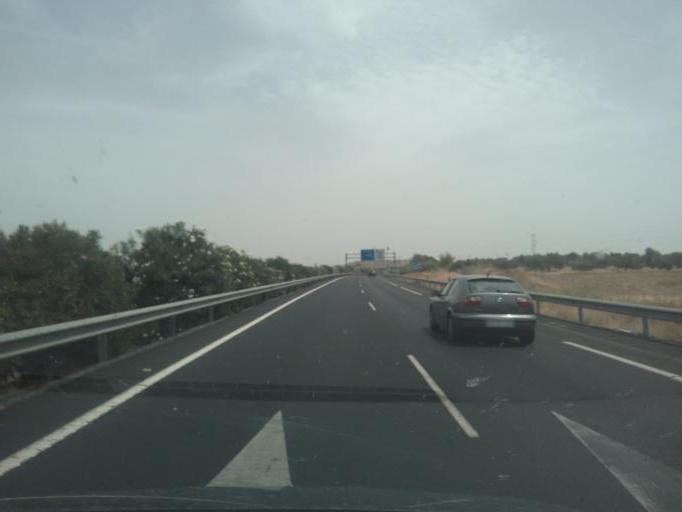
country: ES
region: Andalusia
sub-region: Provincia de Huelva
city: Bonares
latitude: 37.3424
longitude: -6.6831
